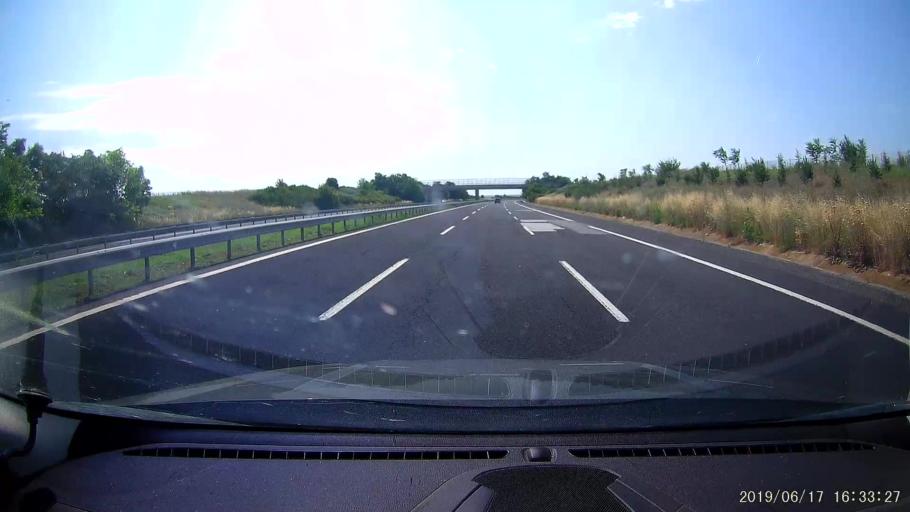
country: TR
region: Kirklareli
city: Buyukkaristiran
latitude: 41.3812
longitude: 27.5723
